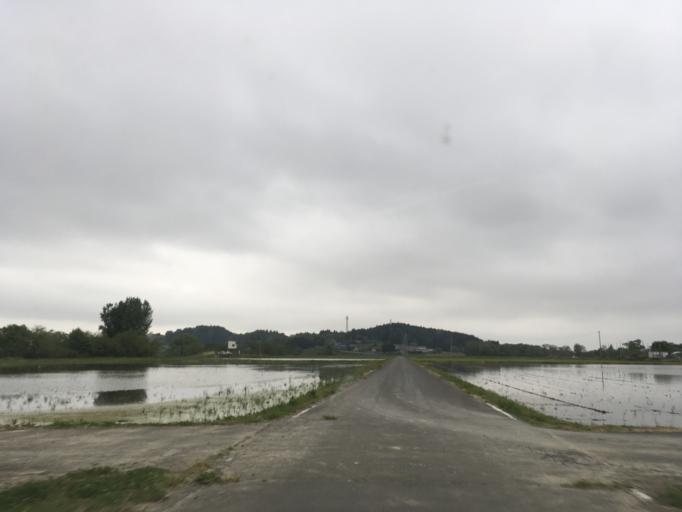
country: JP
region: Miyagi
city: Wakuya
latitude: 38.7162
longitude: 141.2898
